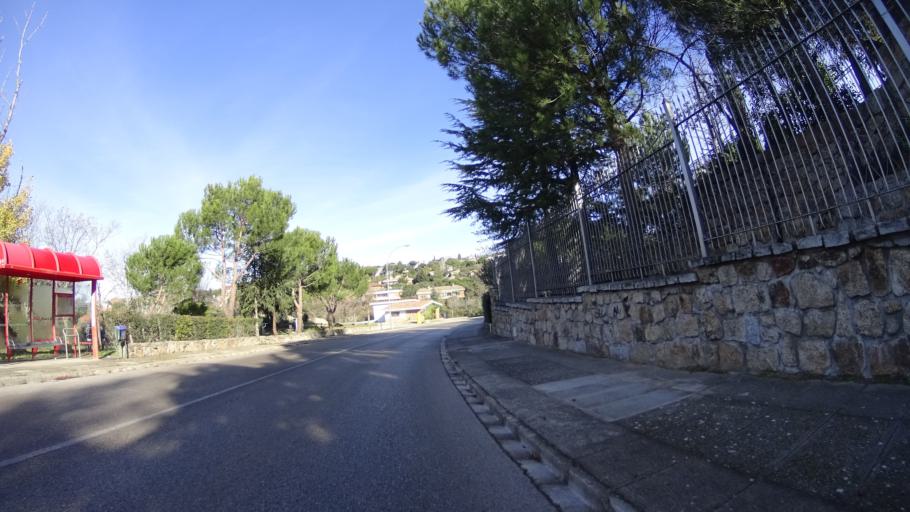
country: ES
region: Madrid
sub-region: Provincia de Madrid
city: Torrelodones
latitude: 40.6035
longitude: -3.9400
